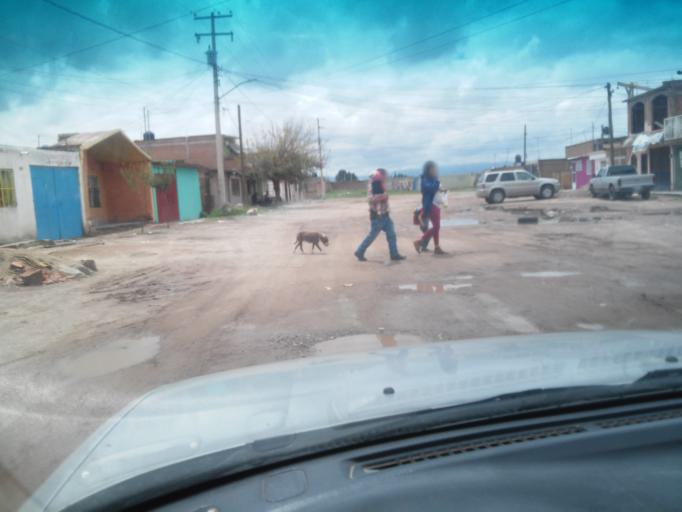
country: MX
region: Durango
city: Victoria de Durango
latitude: 24.0118
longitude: -104.6224
